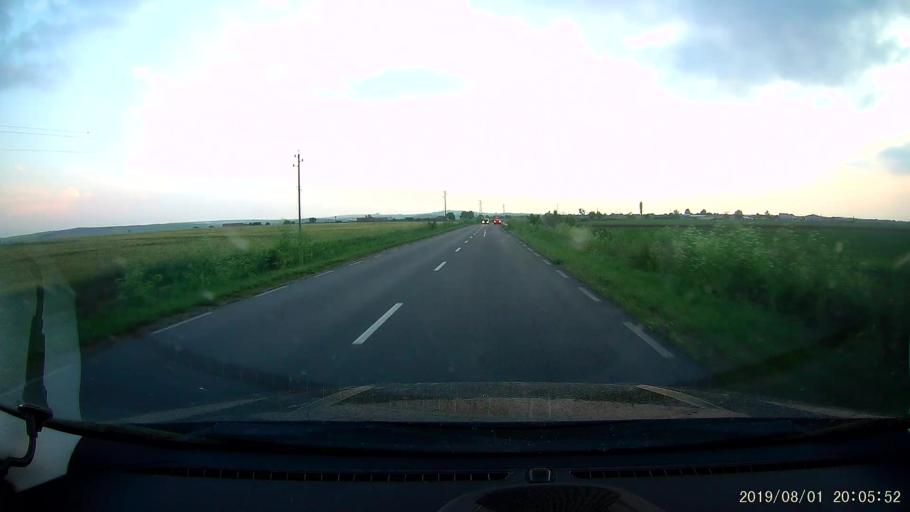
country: BG
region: Yambol
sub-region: Obshtina Yambol
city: Yambol
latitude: 42.5396
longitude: 26.5605
